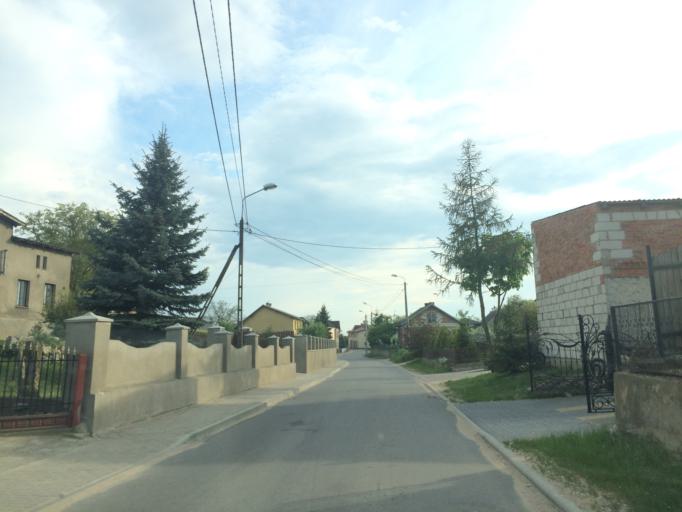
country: PL
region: Kujawsko-Pomorskie
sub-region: Powiat brodnicki
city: Brzozie
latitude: 53.3577
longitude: 19.7088
